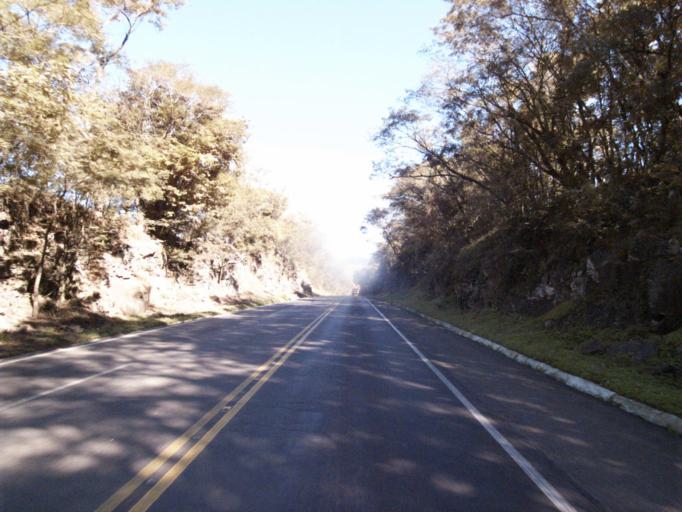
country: BR
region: Rio Grande do Sul
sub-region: Frederico Westphalen
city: Frederico Westphalen
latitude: -26.7987
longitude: -53.3074
